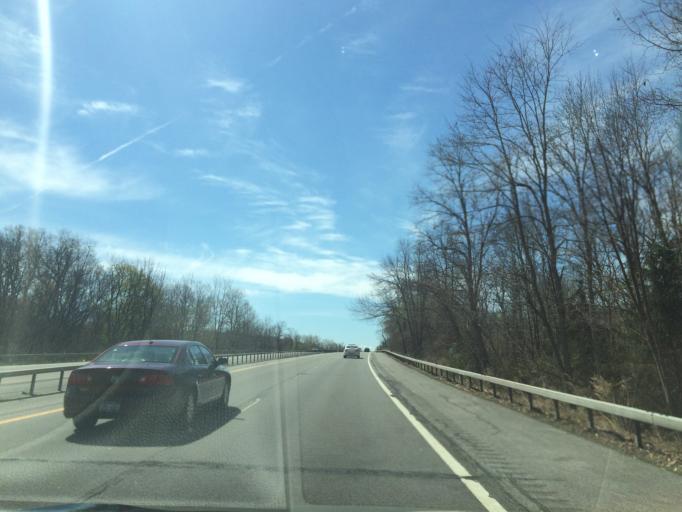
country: US
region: New York
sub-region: Monroe County
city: East Rochester
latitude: 43.0668
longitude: -77.4731
